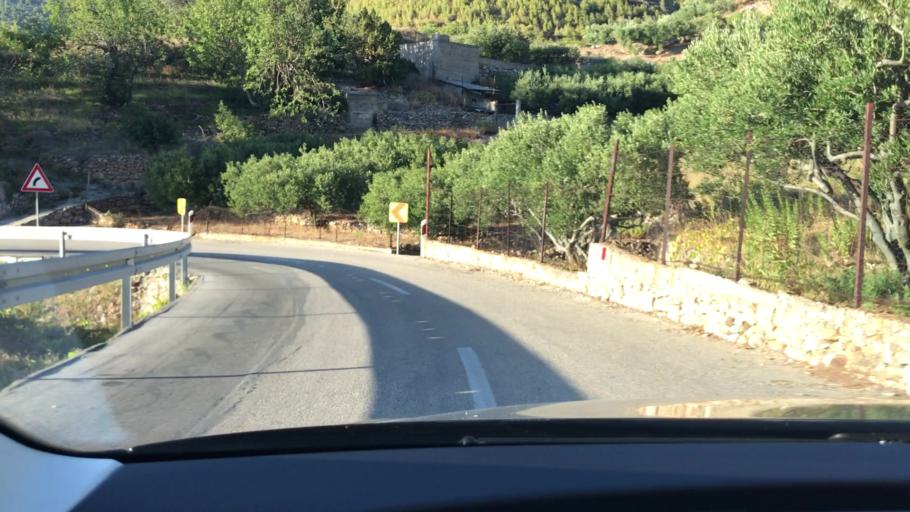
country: HR
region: Splitsko-Dalmatinska
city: Komiza
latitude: 43.0418
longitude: 16.0984
